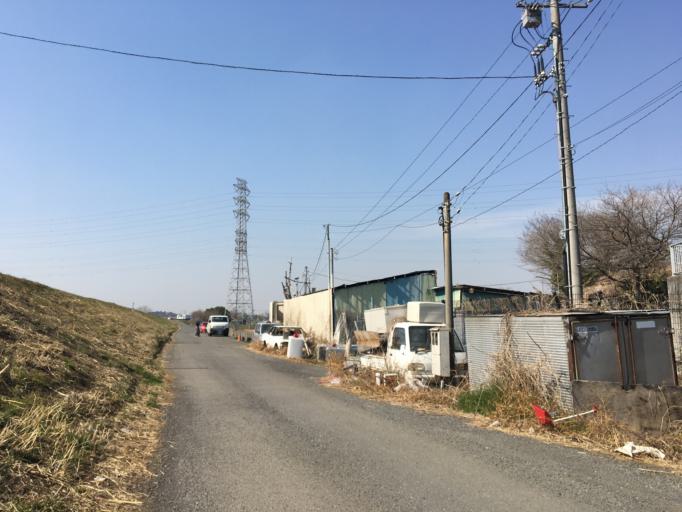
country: JP
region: Saitama
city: Shiki
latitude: 35.8264
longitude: 139.5983
